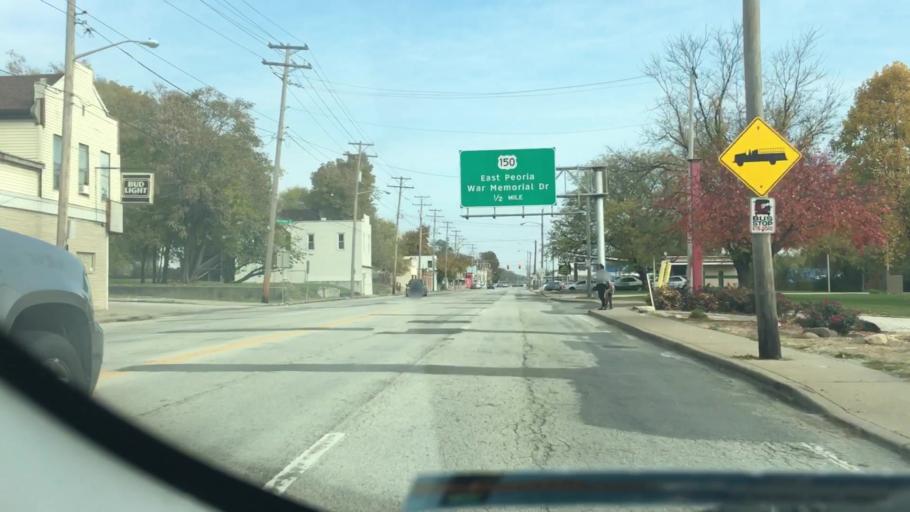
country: US
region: Illinois
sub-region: Peoria County
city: North Peoria
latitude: 40.7154
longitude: -89.5603
